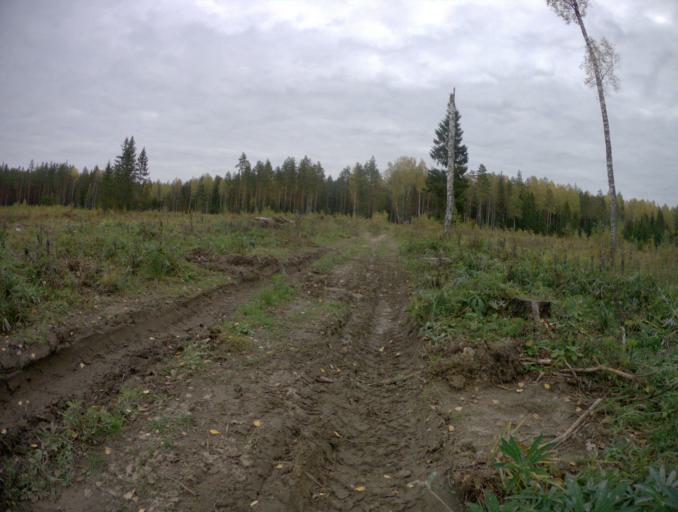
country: RU
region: Vladimir
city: Stepantsevo
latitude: 56.3114
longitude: 41.5687
